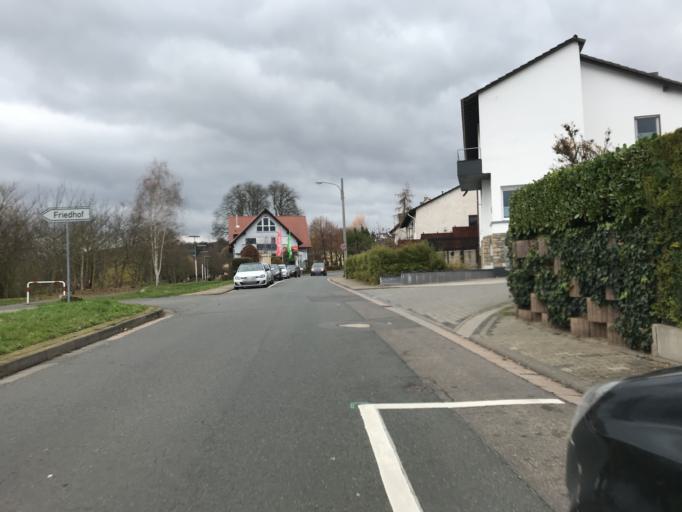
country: DE
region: Rheinland-Pfalz
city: Gau-Bischofsheim
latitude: 49.9157
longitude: 8.2826
